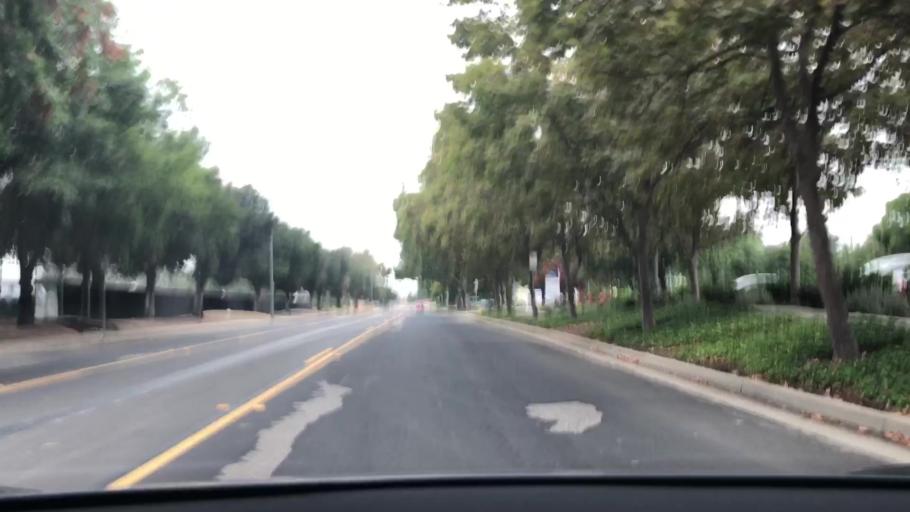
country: US
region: California
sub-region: Santa Clara County
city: Seven Trees
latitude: 37.2365
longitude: -121.7857
